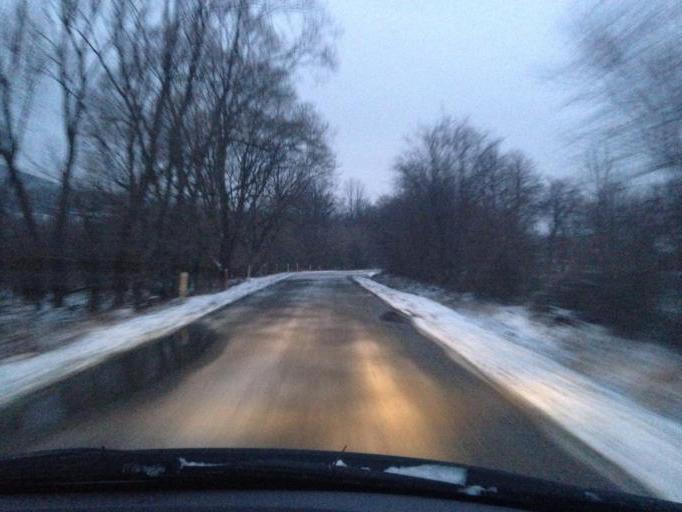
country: PL
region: Subcarpathian Voivodeship
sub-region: Powiat jasielski
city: Krempna
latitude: 49.5299
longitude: 21.5533
